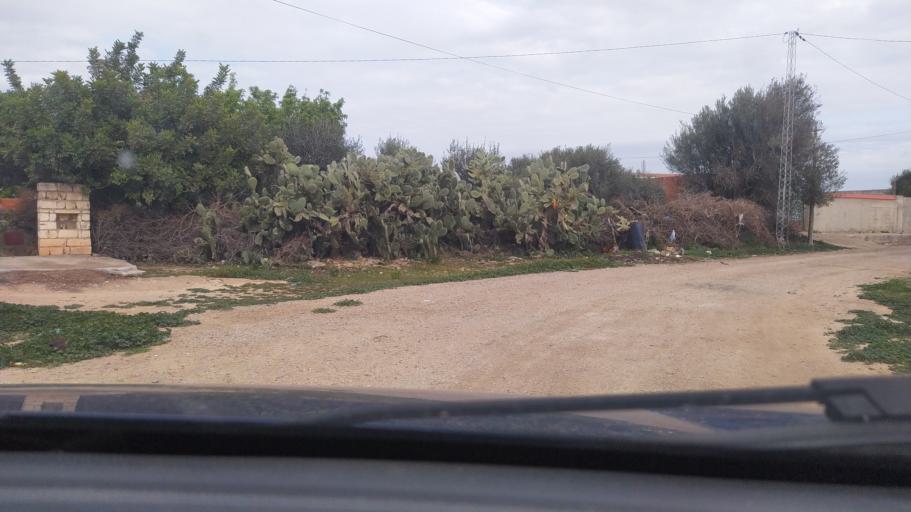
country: TN
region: Al Munastir
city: Sidi Bin Nur
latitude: 35.5169
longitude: 10.9248
